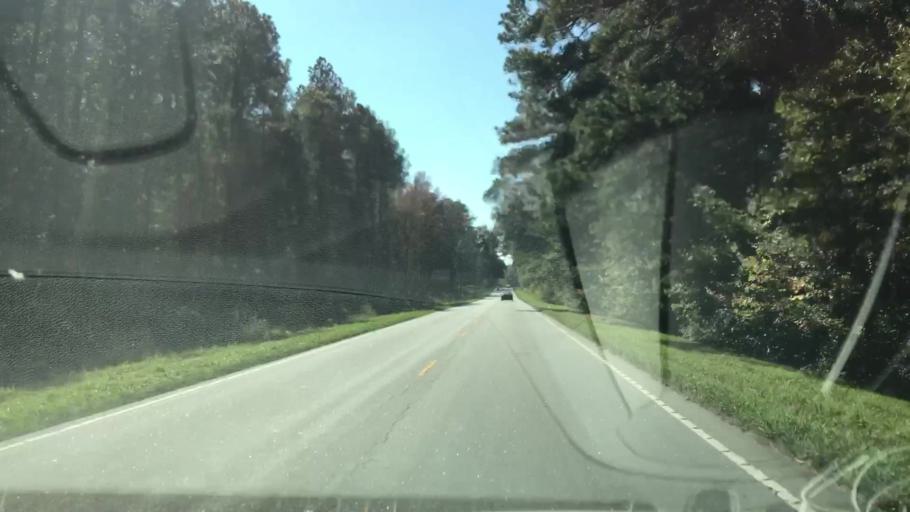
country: US
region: South Carolina
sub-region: Jasper County
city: Ridgeland
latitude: 32.3997
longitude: -80.9067
